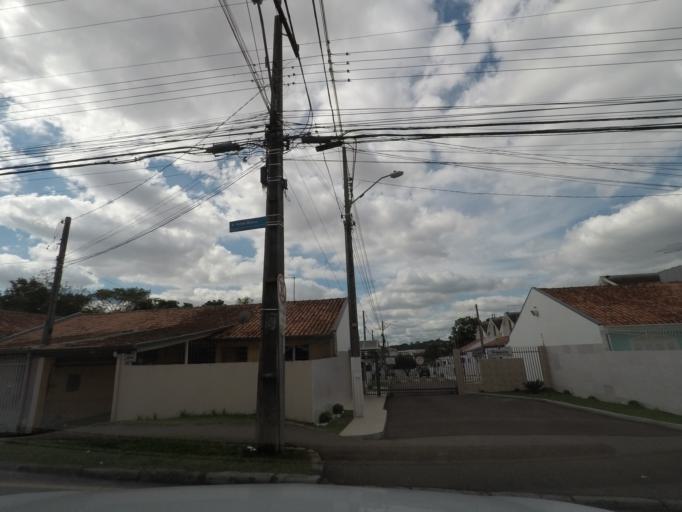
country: BR
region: Parana
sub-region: Sao Jose Dos Pinhais
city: Sao Jose dos Pinhais
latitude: -25.4881
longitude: -49.2266
